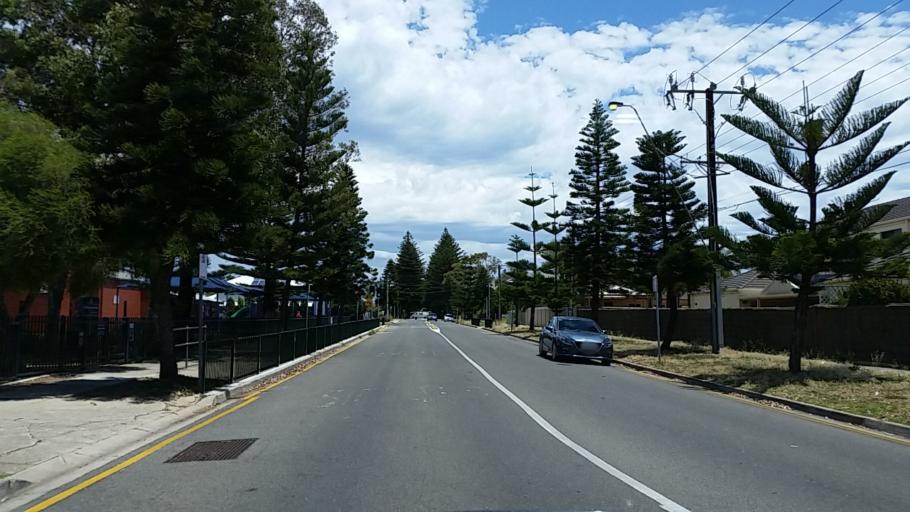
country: AU
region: South Australia
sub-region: Charles Sturt
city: Grange
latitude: -34.9021
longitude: 138.4974
